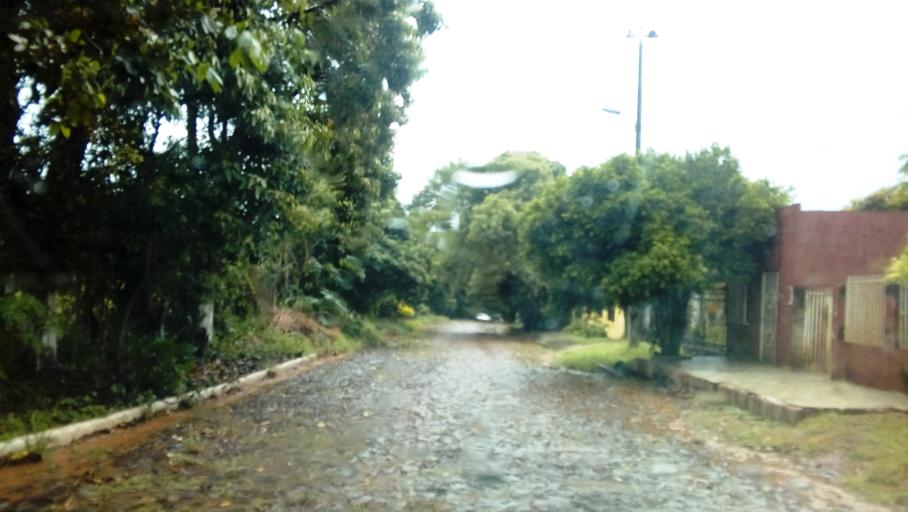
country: PY
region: Alto Parana
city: Ciudad del Este
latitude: -25.4179
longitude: -54.6405
